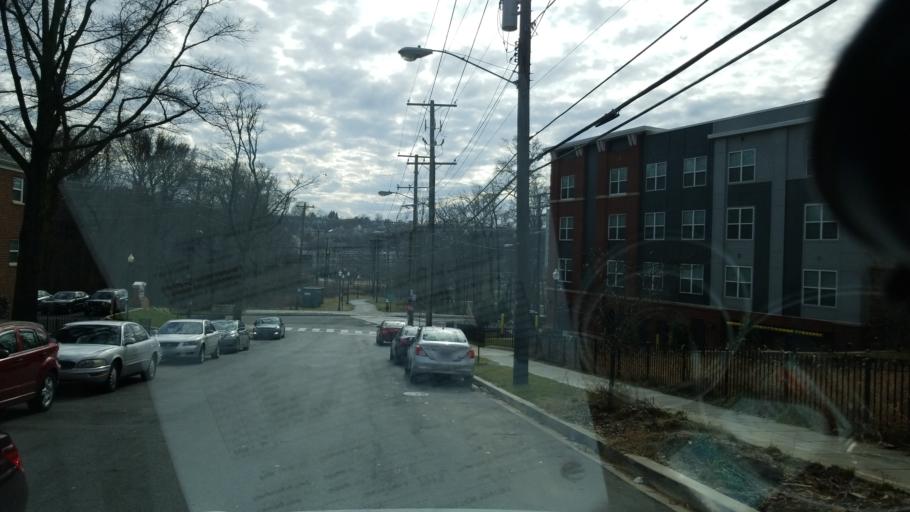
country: US
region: Maryland
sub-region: Prince George's County
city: Glassmanor
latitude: 38.8405
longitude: -76.9885
